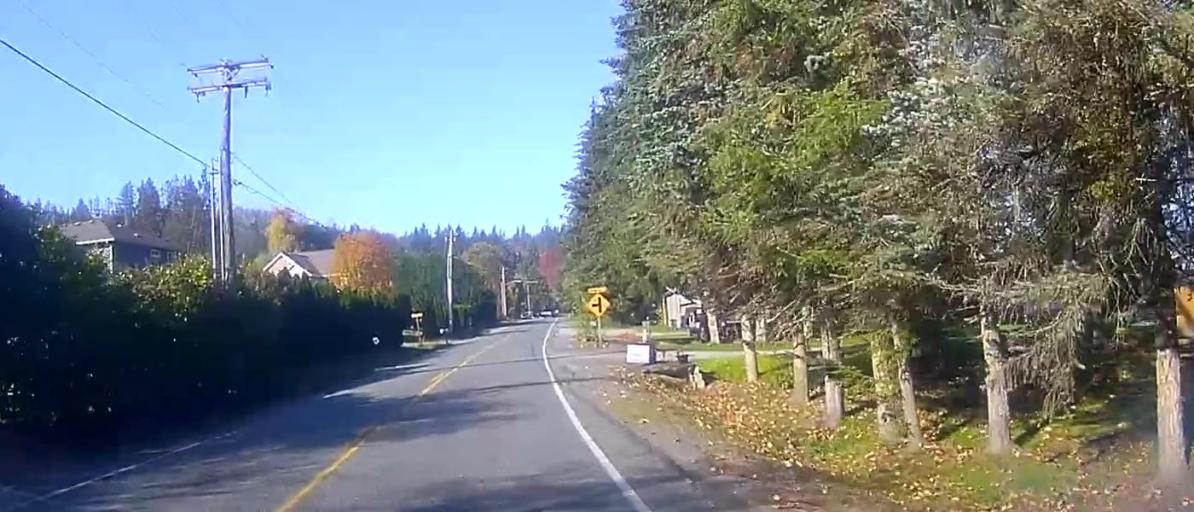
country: US
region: Washington
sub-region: Skagit County
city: Big Lake
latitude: 48.3895
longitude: -122.2452
